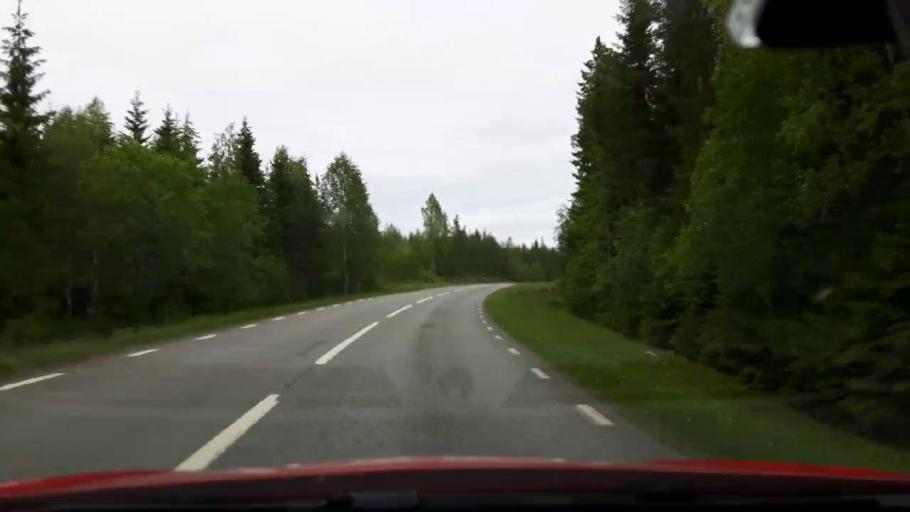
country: SE
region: Jaemtland
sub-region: Stroemsunds Kommun
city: Stroemsund
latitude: 63.4225
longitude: 15.5372
